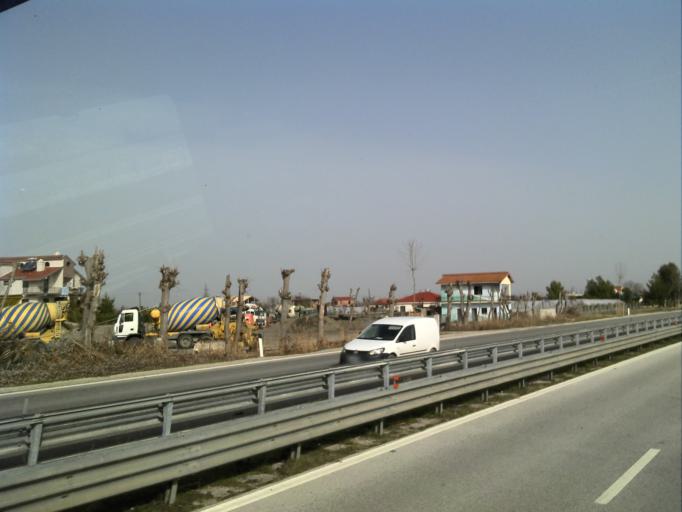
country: AL
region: Fier
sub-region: Rrethi i Lushnjes
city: Krutja e Poshtme
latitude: 40.8683
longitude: 19.6558
